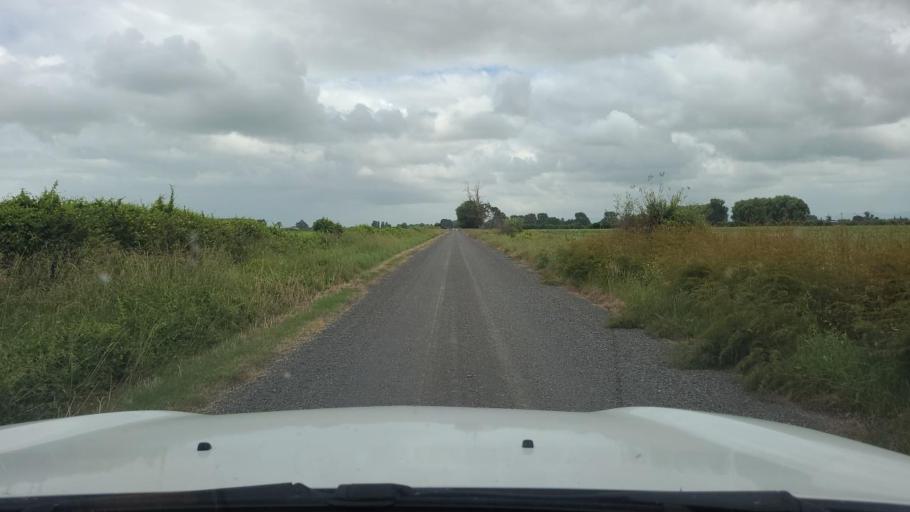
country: NZ
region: Bay of Plenty
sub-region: Western Bay of Plenty District
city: Katikati
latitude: -37.5846
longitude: 175.7130
